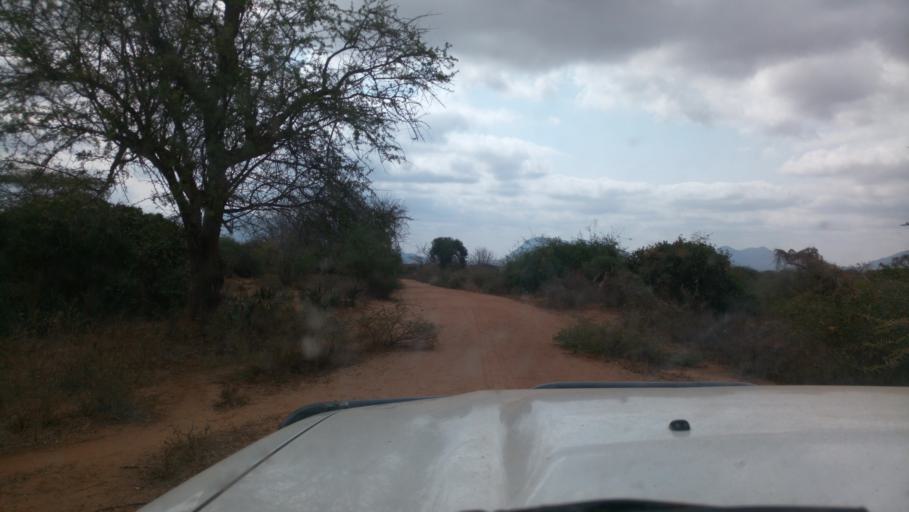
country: KE
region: Kitui
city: Kitui
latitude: -1.8343
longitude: 38.3067
